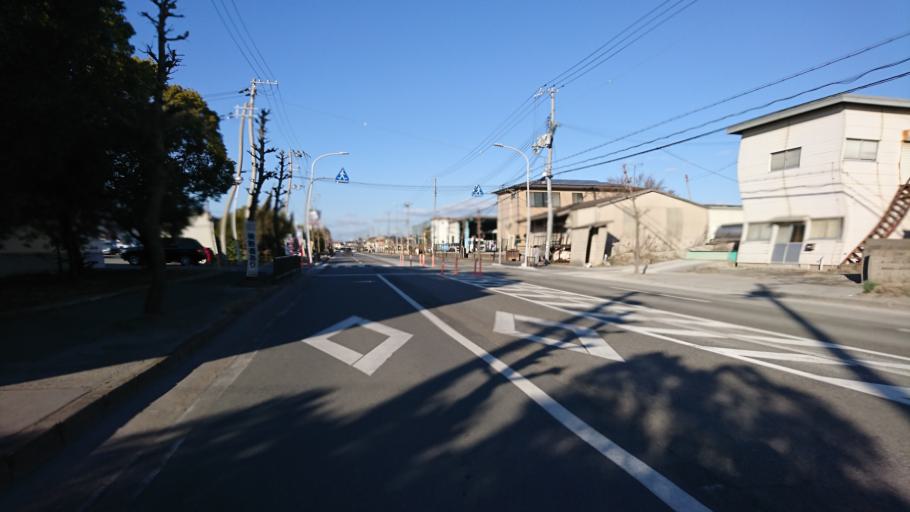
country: JP
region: Hyogo
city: Kakogawacho-honmachi
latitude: 34.7345
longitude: 134.8218
